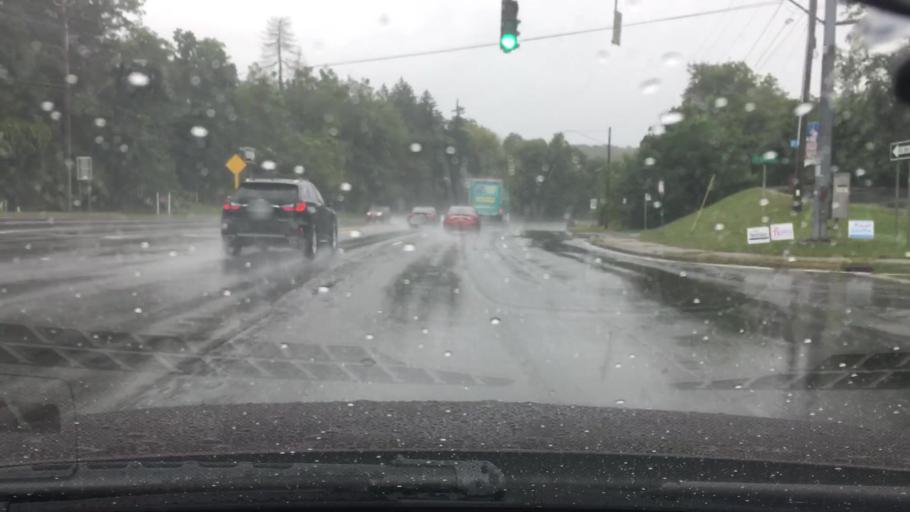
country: US
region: New York
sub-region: Dutchess County
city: Spackenkill
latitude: 41.6428
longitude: -73.9207
